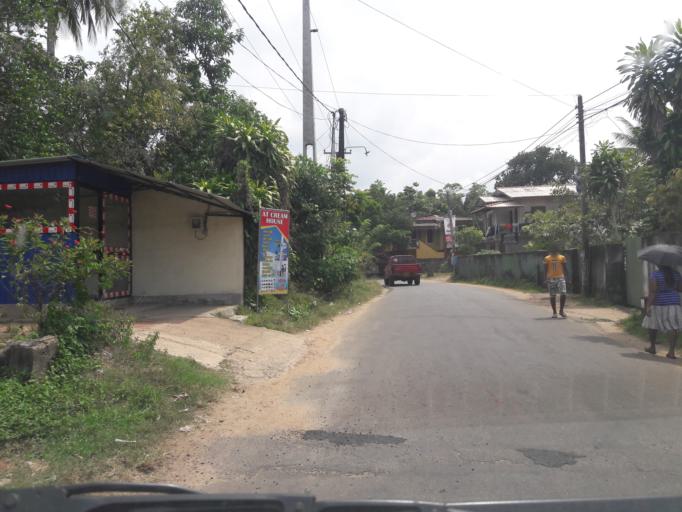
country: LK
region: Southern
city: Hikkaduwa
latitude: 6.0943
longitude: 80.1458
